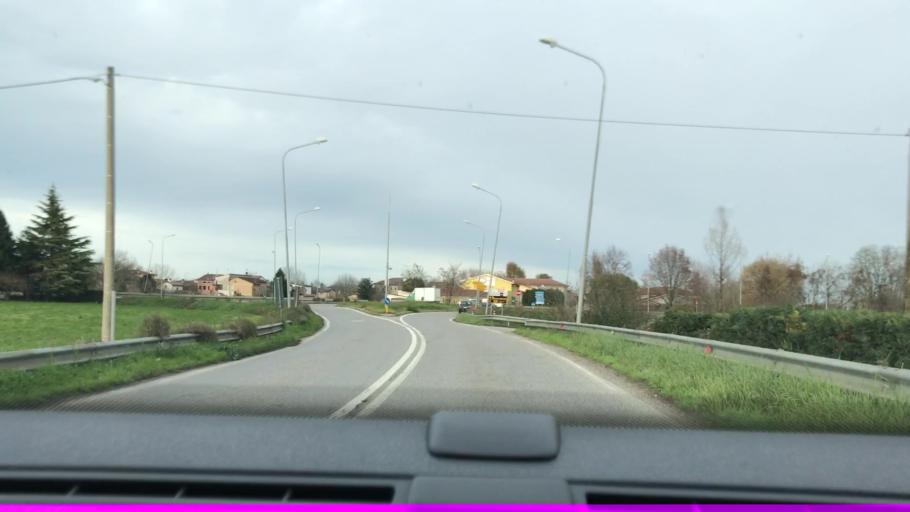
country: IT
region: Lombardy
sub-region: Provincia di Mantova
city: San Benedetto Po
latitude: 45.0307
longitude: 10.9373
